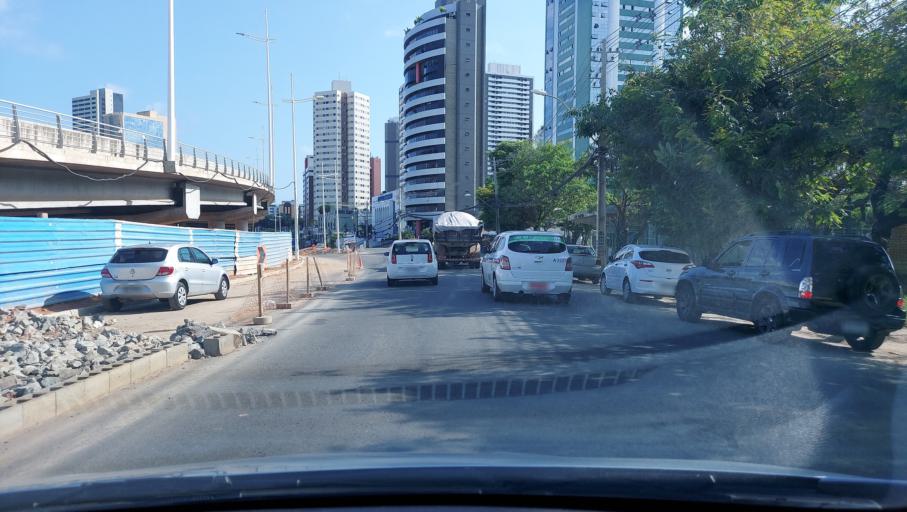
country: BR
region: Bahia
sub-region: Salvador
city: Salvador
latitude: -12.9833
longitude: -38.4669
